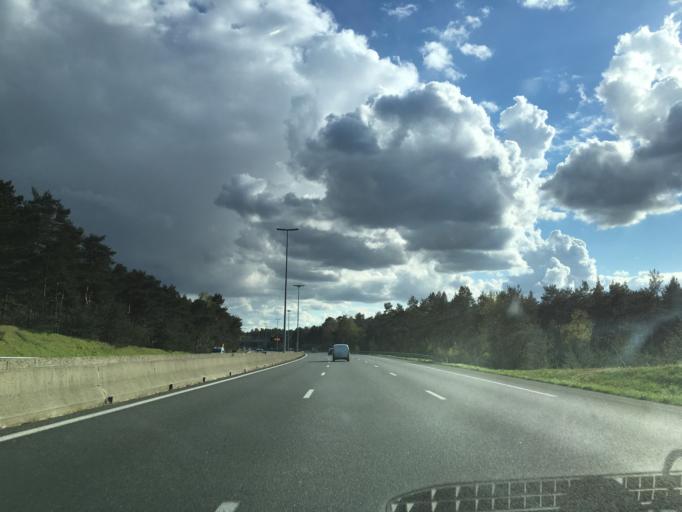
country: FR
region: Picardie
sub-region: Departement de l'Oise
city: Senlis
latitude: 49.1762
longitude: 2.6022
